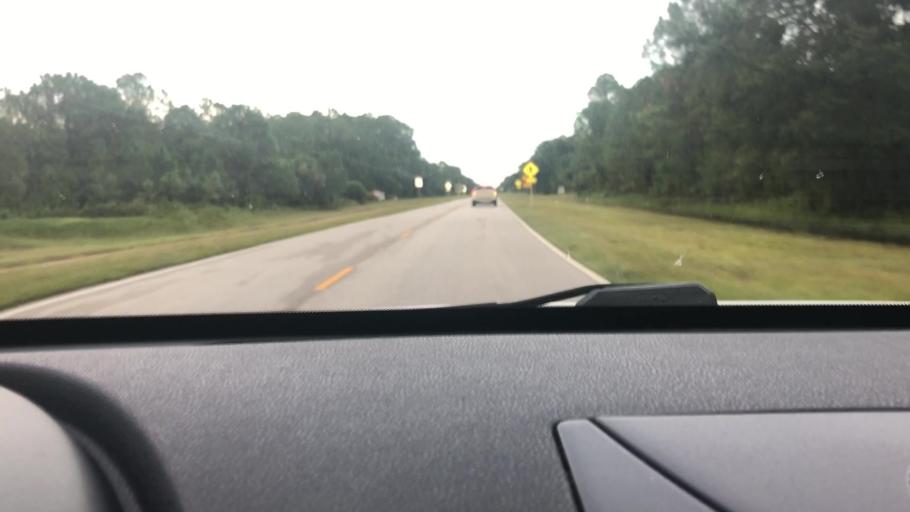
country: US
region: Florida
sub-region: Charlotte County
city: Port Charlotte
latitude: 27.0690
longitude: -82.1354
